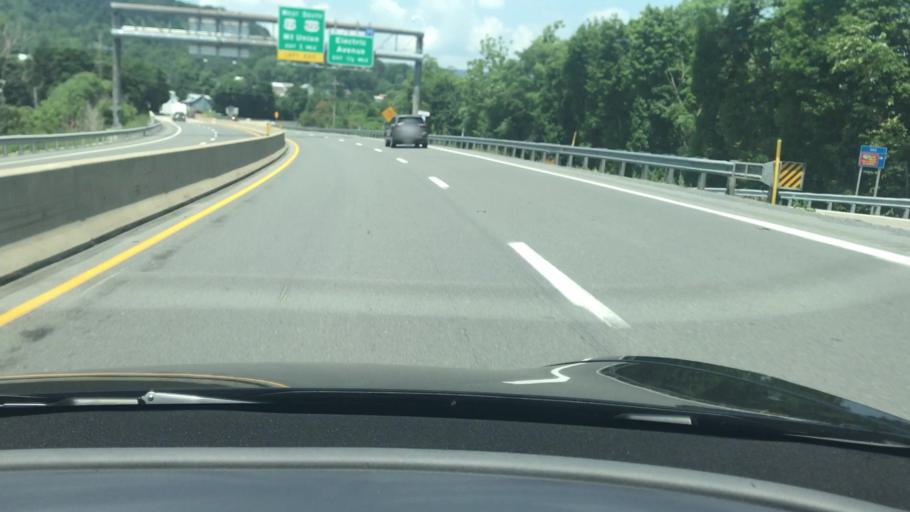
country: US
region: Pennsylvania
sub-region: Mifflin County
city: Lewistown
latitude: 40.6045
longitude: -77.5635
